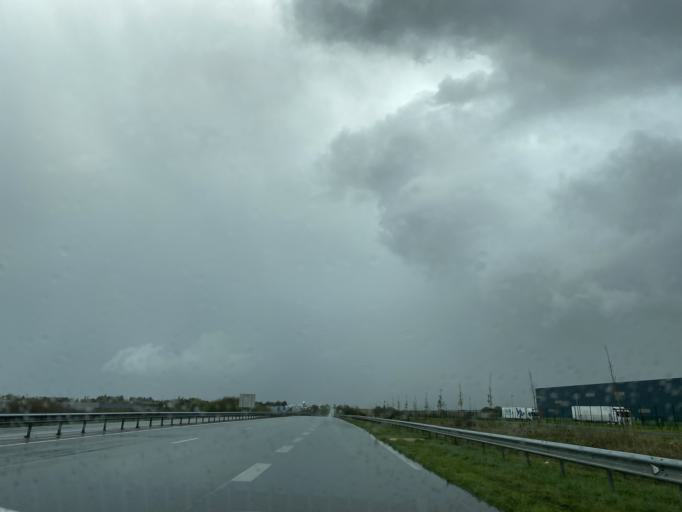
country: FR
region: Centre
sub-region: Departement du Cher
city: La Chapelle-Saint-Ursin
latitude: 47.0508
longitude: 2.3459
